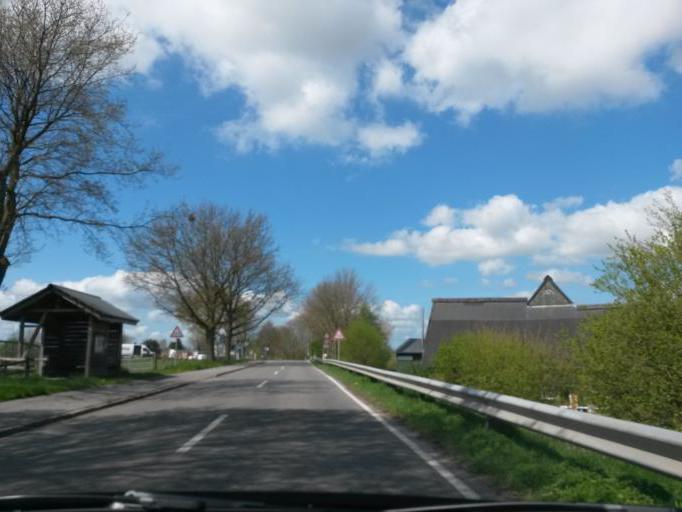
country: DE
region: Schleswig-Holstein
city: Neuendeich
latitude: 53.6753
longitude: 9.6101
